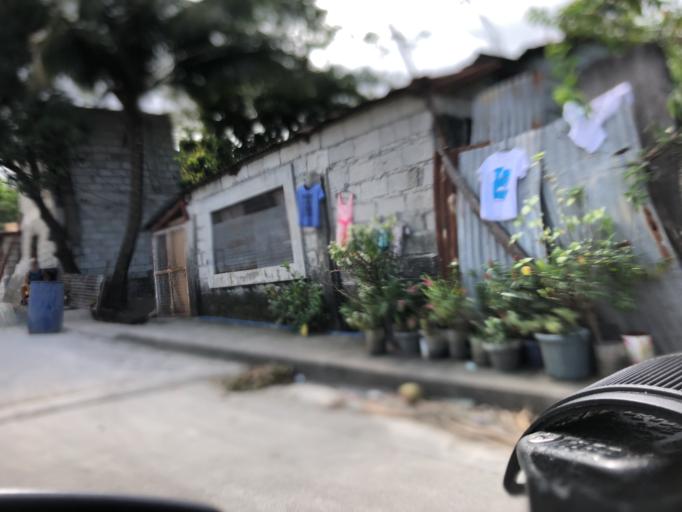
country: PH
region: Central Luzon
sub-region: Province of Bulacan
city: San Jose del Monte
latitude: 14.7648
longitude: 121.0501
